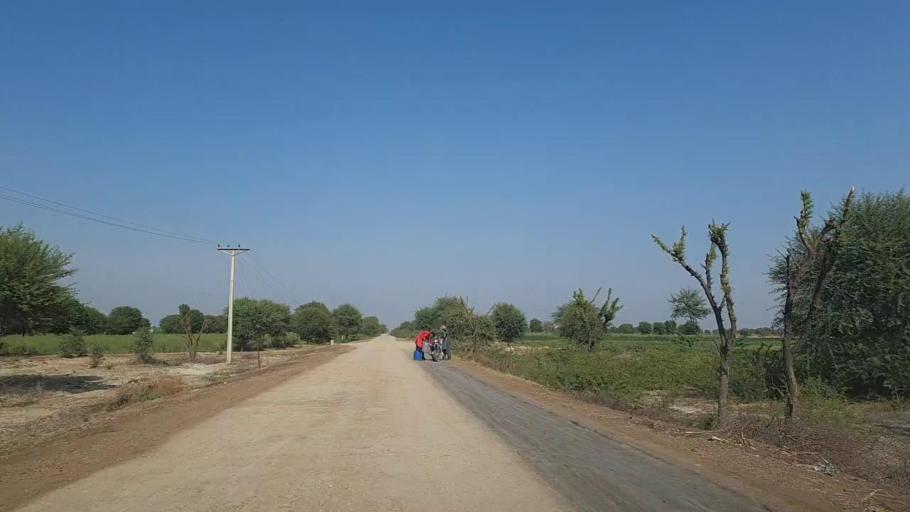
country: PK
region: Sindh
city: Digri
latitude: 25.0899
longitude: 69.2012
